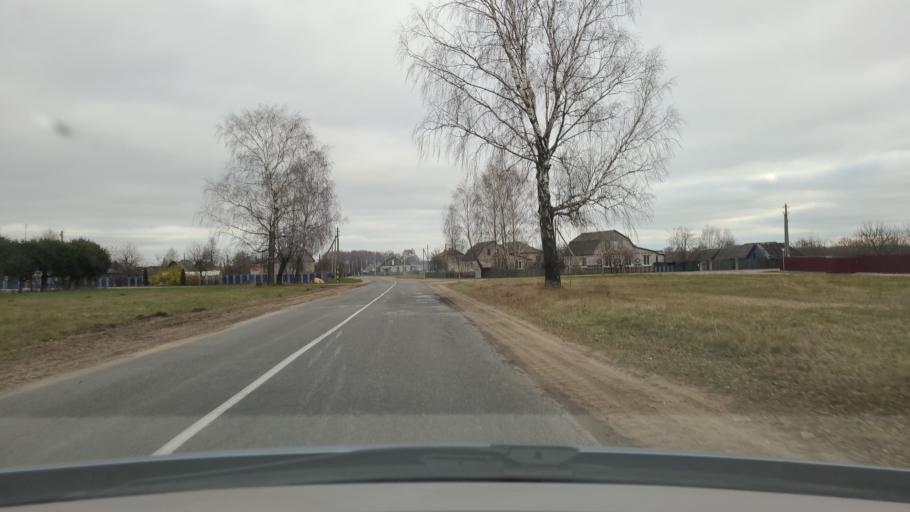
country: BY
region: Minsk
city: Khalopyenichy
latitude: 54.4705
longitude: 28.9780
